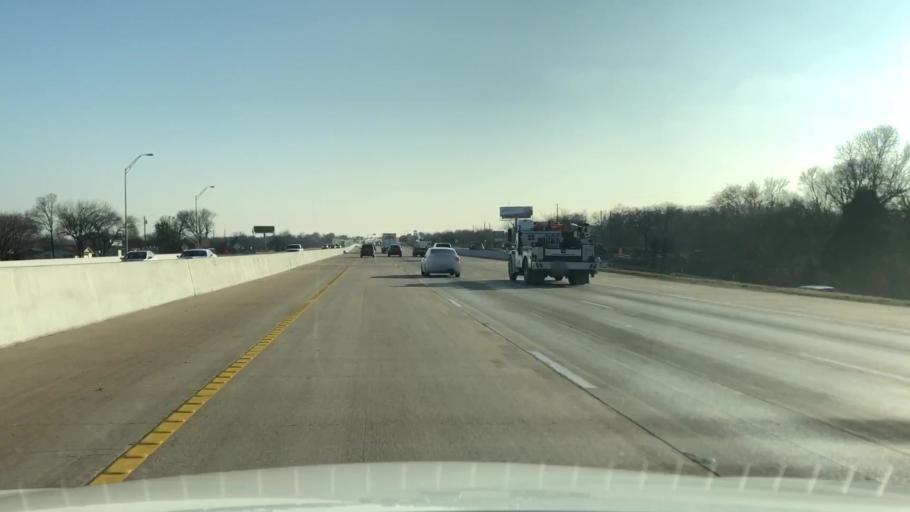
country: US
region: Texas
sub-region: Ellis County
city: Red Oak
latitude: 32.5116
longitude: -96.8223
